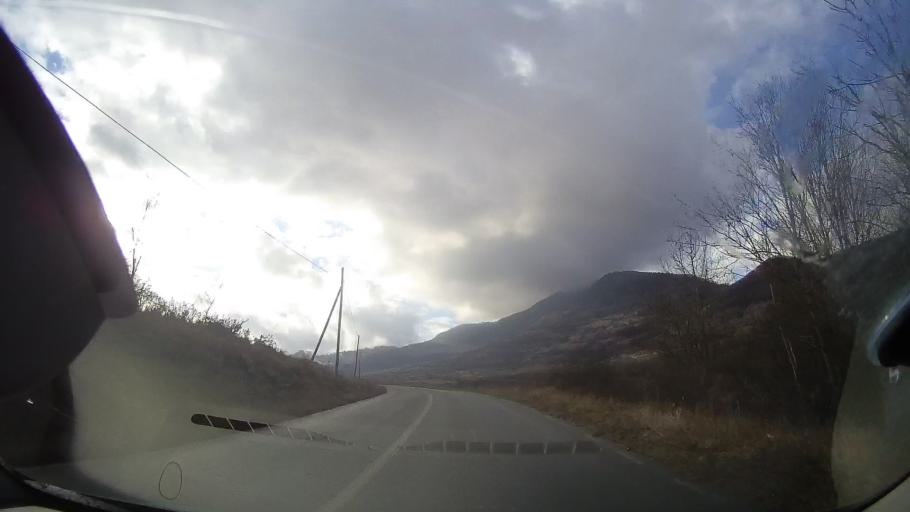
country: RO
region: Alba
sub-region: Comuna Rimetea
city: Rimetea
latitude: 46.4661
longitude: 23.5758
